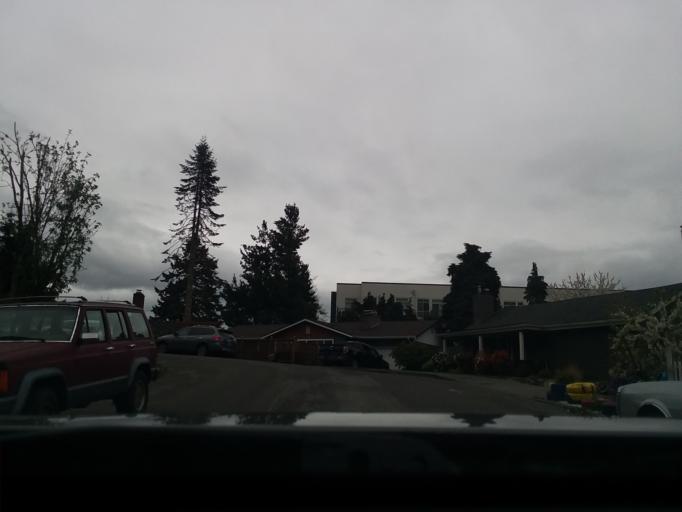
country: US
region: Washington
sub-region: King County
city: Shoreline
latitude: 47.7402
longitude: -122.3427
